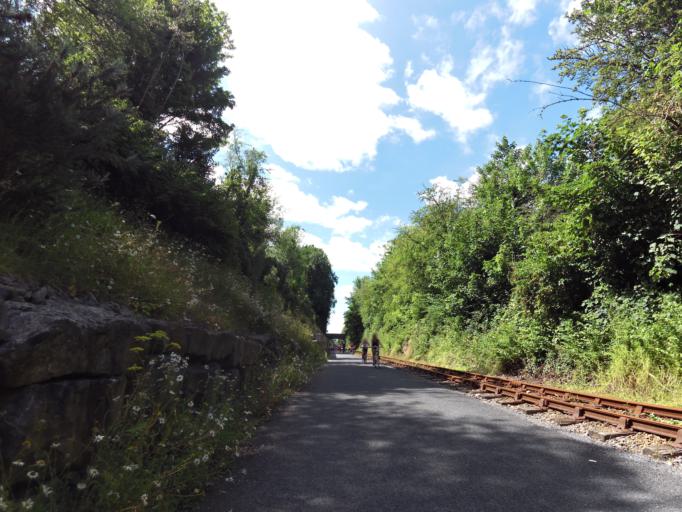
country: IE
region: Leinster
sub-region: Kilkenny
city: Mooncoin
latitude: 52.2471
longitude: -7.2434
